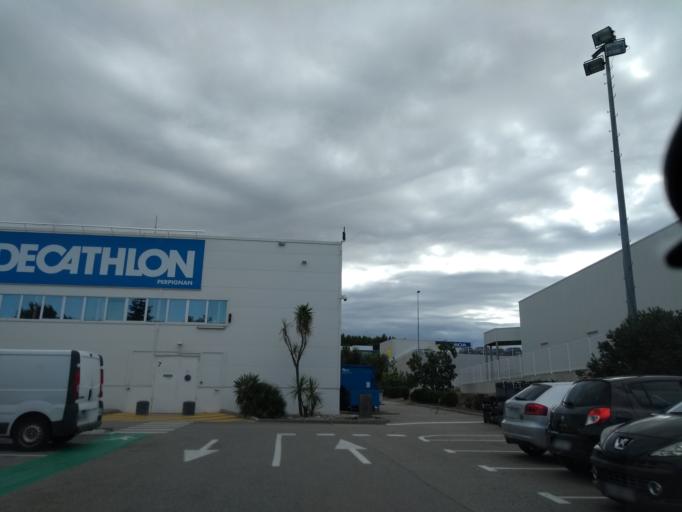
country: FR
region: Languedoc-Roussillon
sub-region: Departement des Pyrenees-Orientales
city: Perpignan
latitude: 42.6727
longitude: 2.8886
